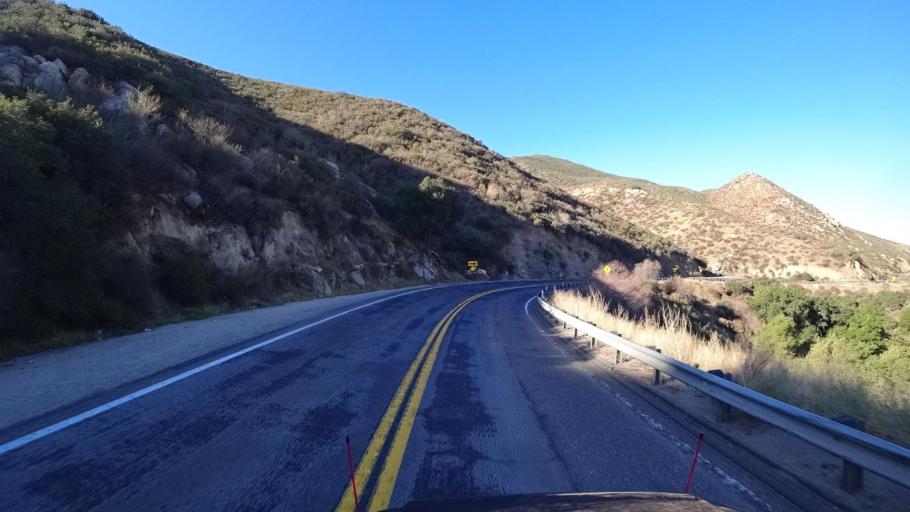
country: MX
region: Baja California
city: Tecate
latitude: 32.5945
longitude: -116.6685
